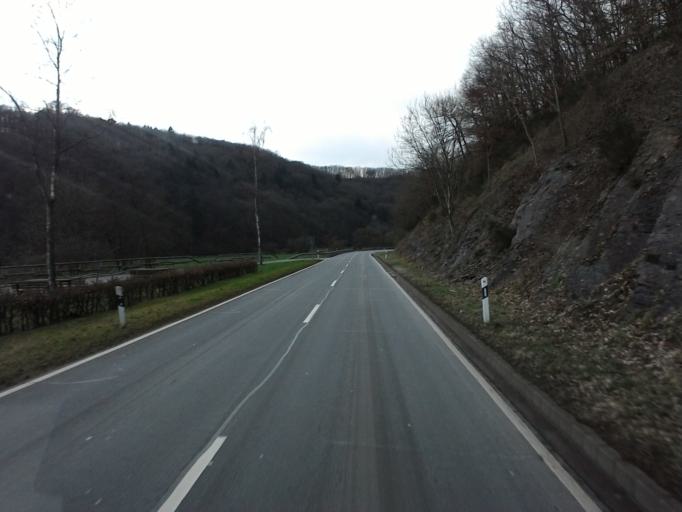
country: DE
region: Rheinland-Pfalz
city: Sinspelt
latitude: 49.9782
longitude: 6.3195
